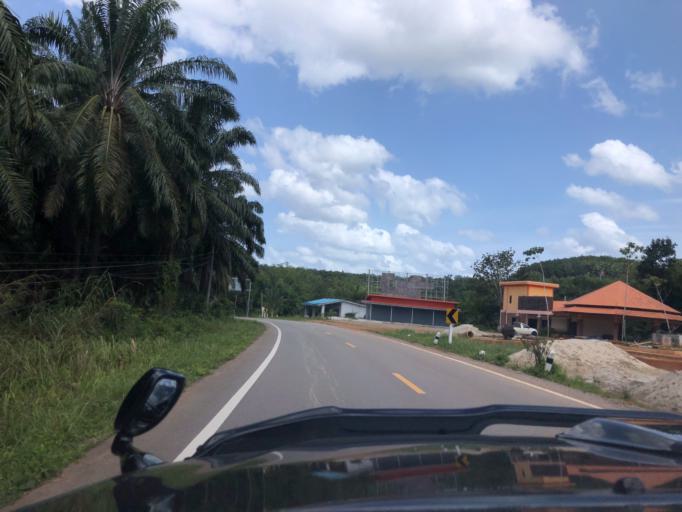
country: TH
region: Krabi
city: Khlong Thom
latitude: 7.9490
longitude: 99.2062
